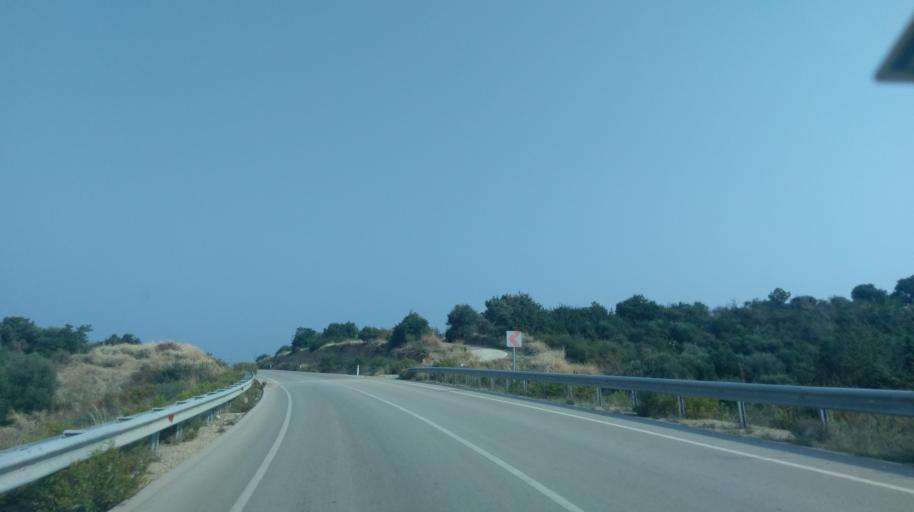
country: CY
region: Ammochostos
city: Trikomo
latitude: 35.4266
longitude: 33.9150
